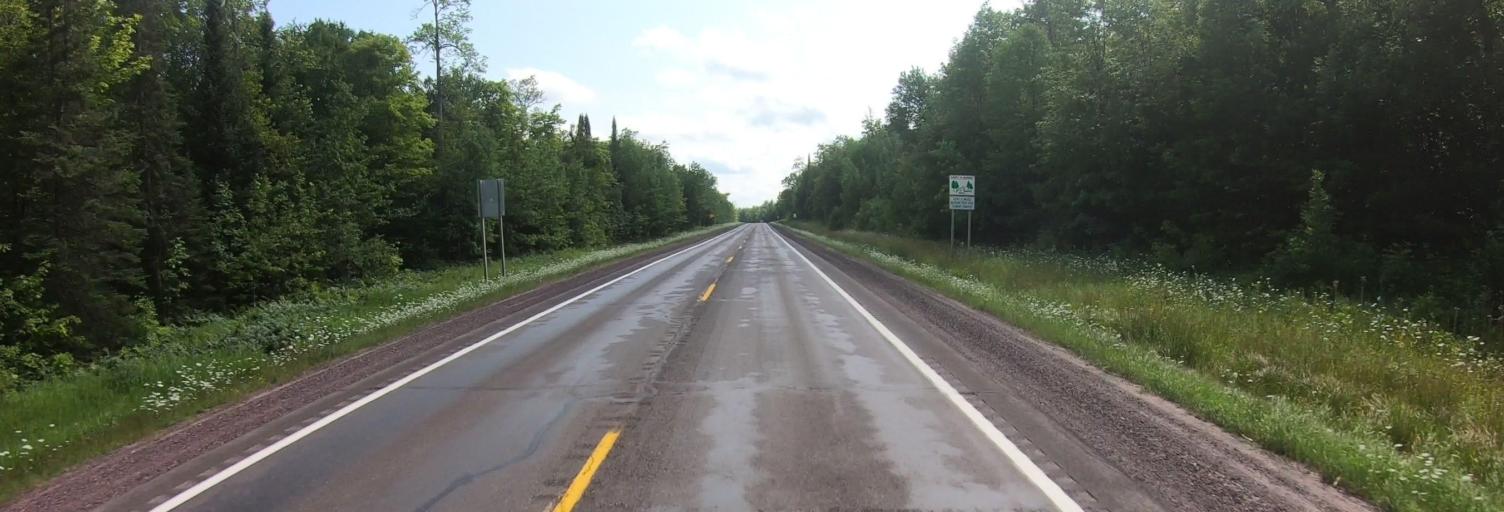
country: US
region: Michigan
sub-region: Ontonagon County
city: Ontonagon
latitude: 46.8352
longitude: -88.9934
